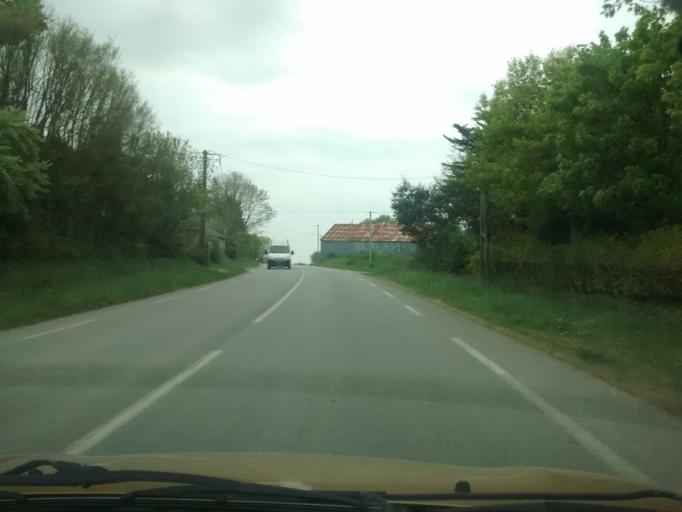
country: FR
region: Brittany
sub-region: Departement du Morbihan
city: Ambon
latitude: 47.5923
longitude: -2.5487
